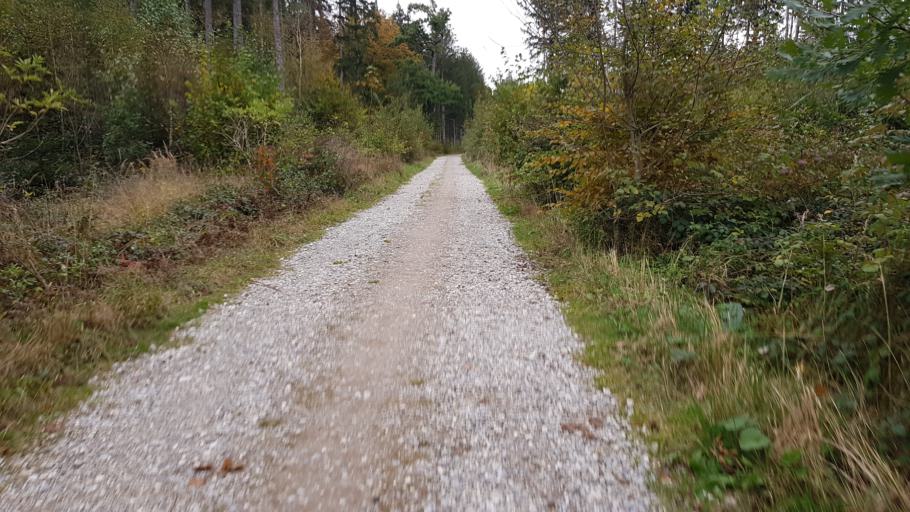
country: DE
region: Bavaria
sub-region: Upper Bavaria
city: Krailling
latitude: 48.1145
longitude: 11.4006
